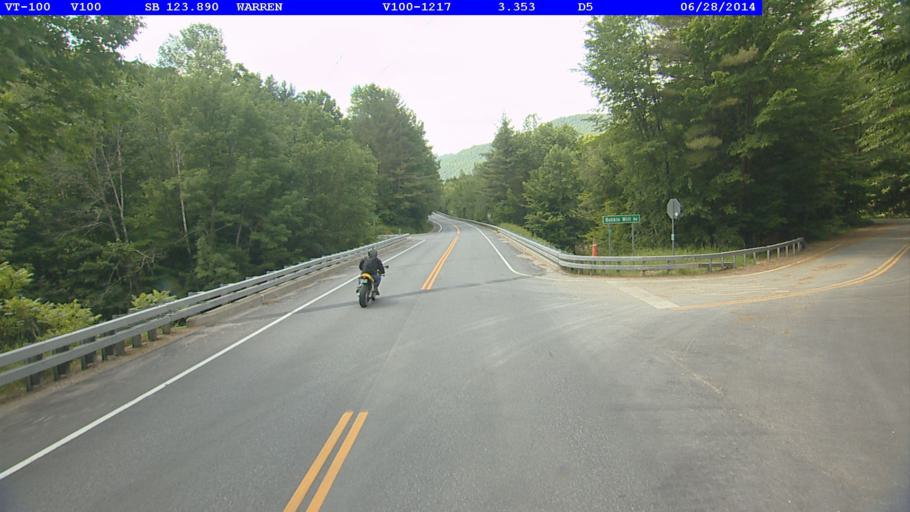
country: US
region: Vermont
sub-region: Washington County
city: Northfield
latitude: 44.1066
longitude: -72.8597
